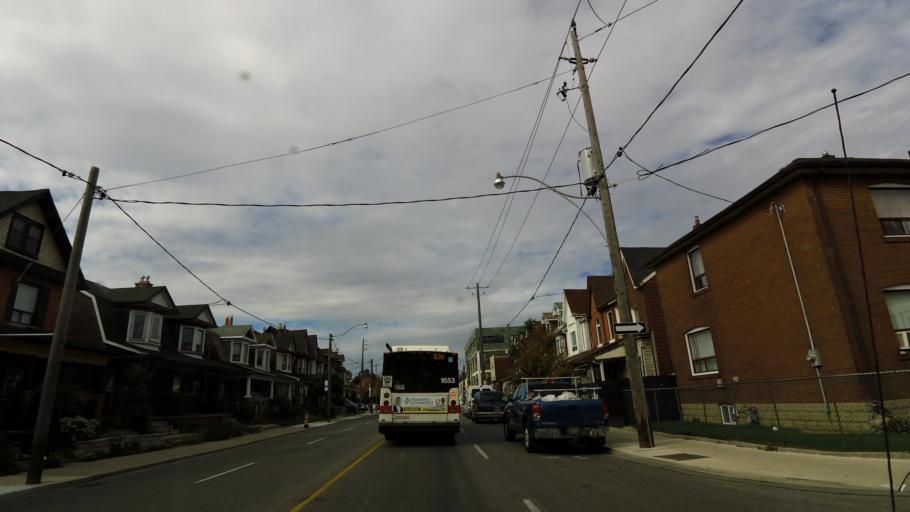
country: CA
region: Ontario
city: Toronto
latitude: 43.6692
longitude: -79.4287
